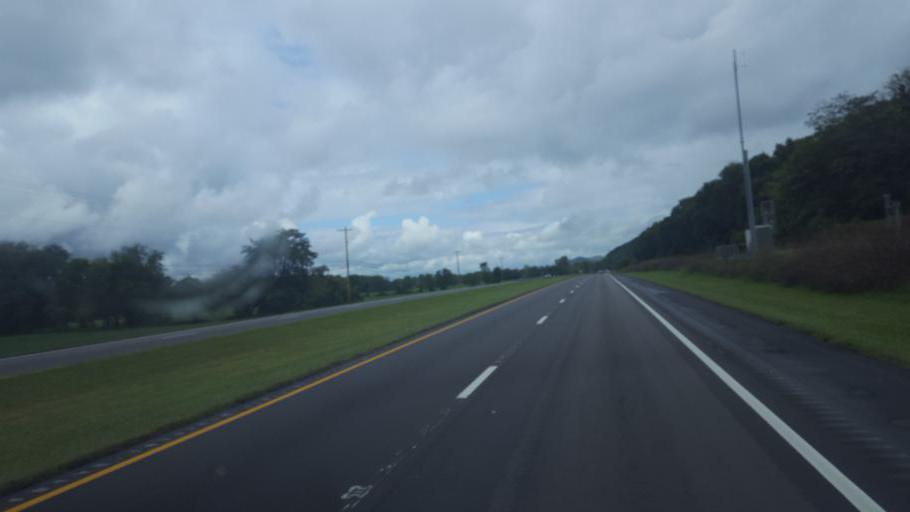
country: US
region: Ohio
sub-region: Scioto County
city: Rosemount
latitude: 38.8276
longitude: -82.9833
